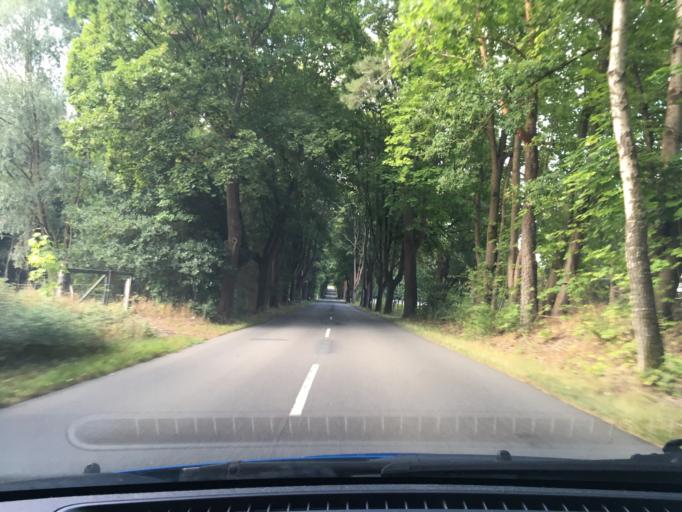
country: DE
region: Lower Saxony
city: Altenmedingen
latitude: 53.1738
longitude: 10.6261
